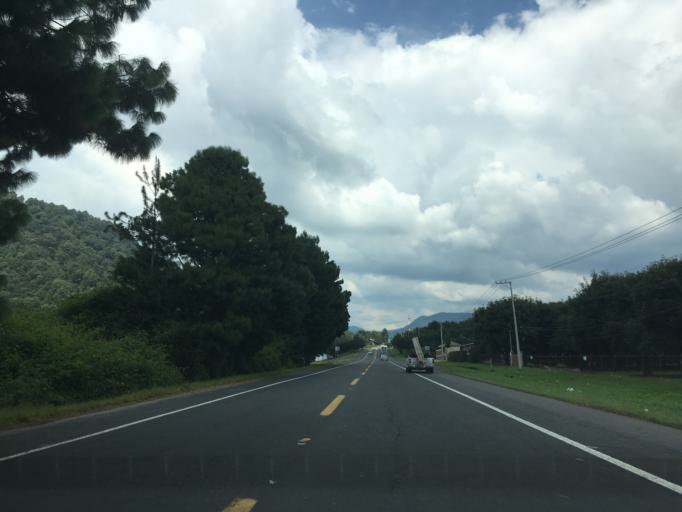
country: MX
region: Michoacan
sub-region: Uruapan
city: Uruapan
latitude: 19.4580
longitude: -102.0761
